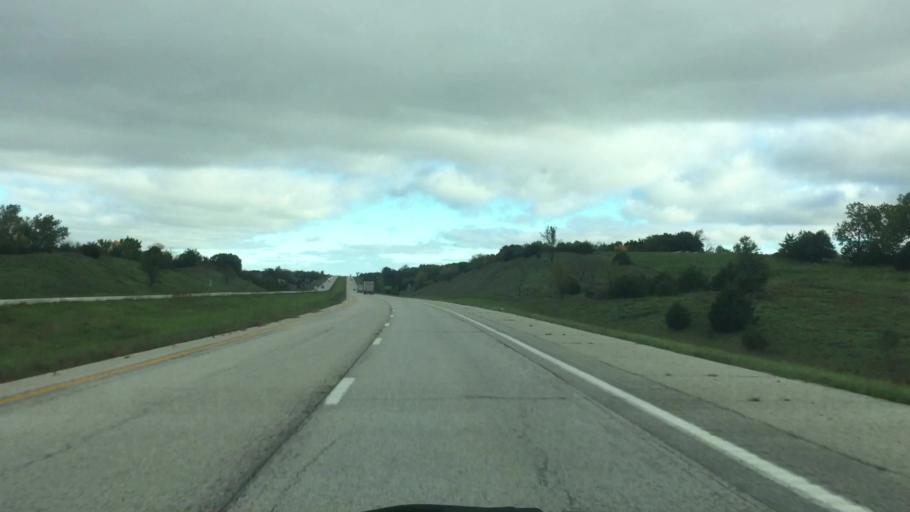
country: US
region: Missouri
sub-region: Harrison County
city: Bethany
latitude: 40.1822
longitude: -94.0147
